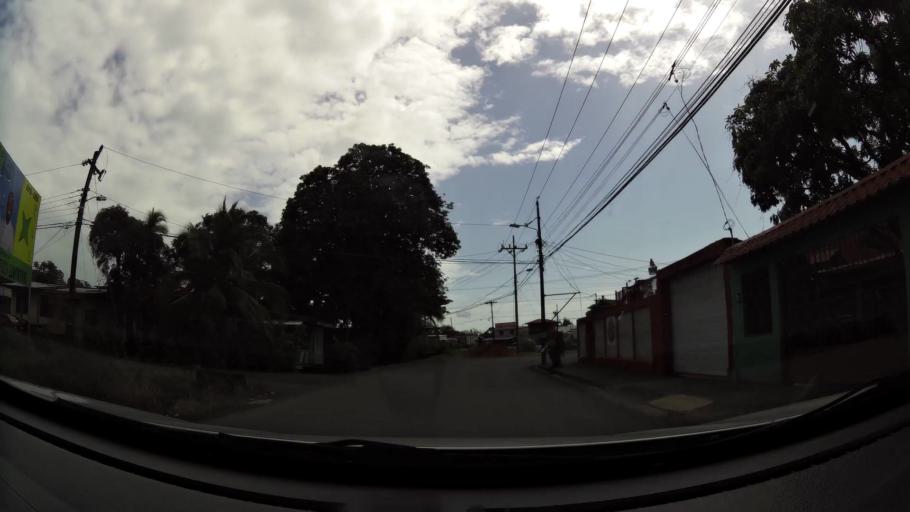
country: CR
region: Limon
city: Limon
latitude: 9.9861
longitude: -83.0467
